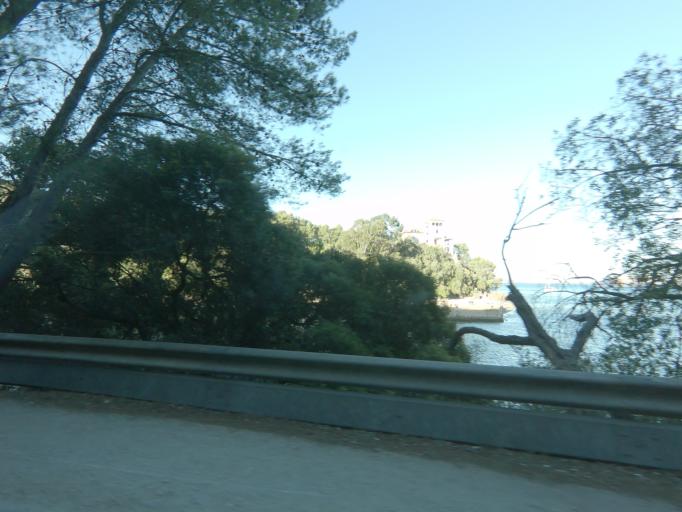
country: PT
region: Setubal
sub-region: Setubal
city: Setubal
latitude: 38.5065
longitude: -8.9267
